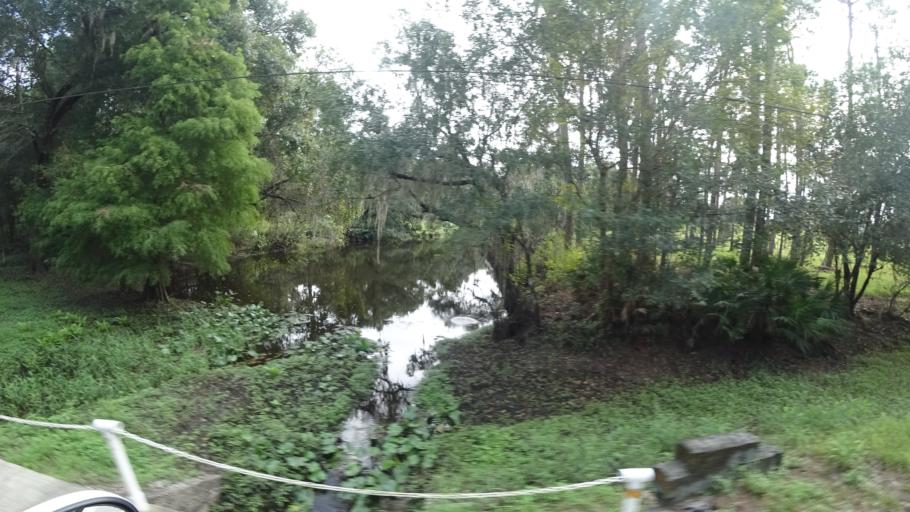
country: US
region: Florida
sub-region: Hillsborough County
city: Wimauma
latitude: 27.5931
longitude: -82.3379
